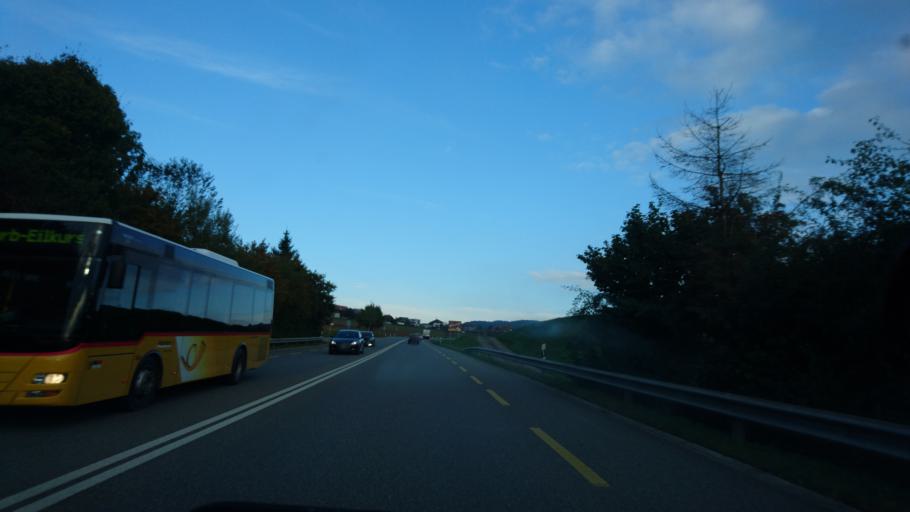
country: CH
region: Bern
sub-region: Bern-Mittelland District
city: Biglen
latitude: 46.9176
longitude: 7.6030
